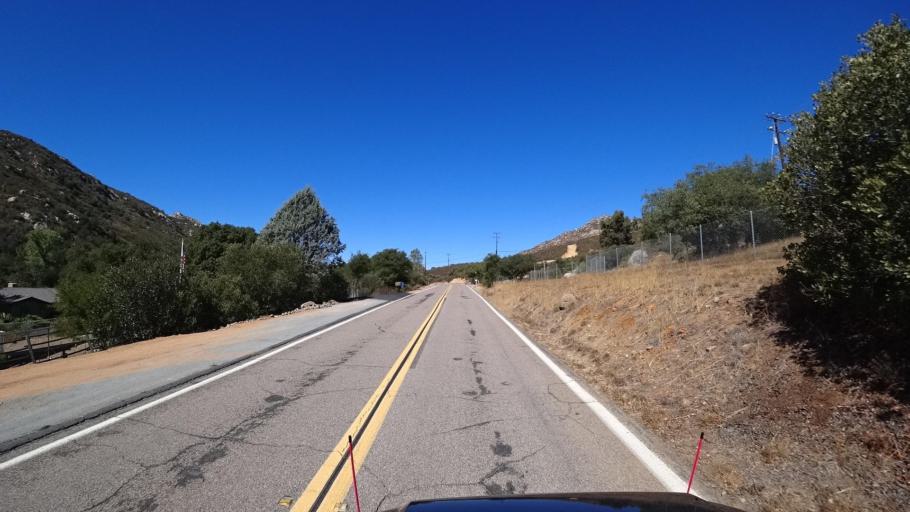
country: US
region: California
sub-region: San Diego County
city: Alpine
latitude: 32.7061
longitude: -116.7331
